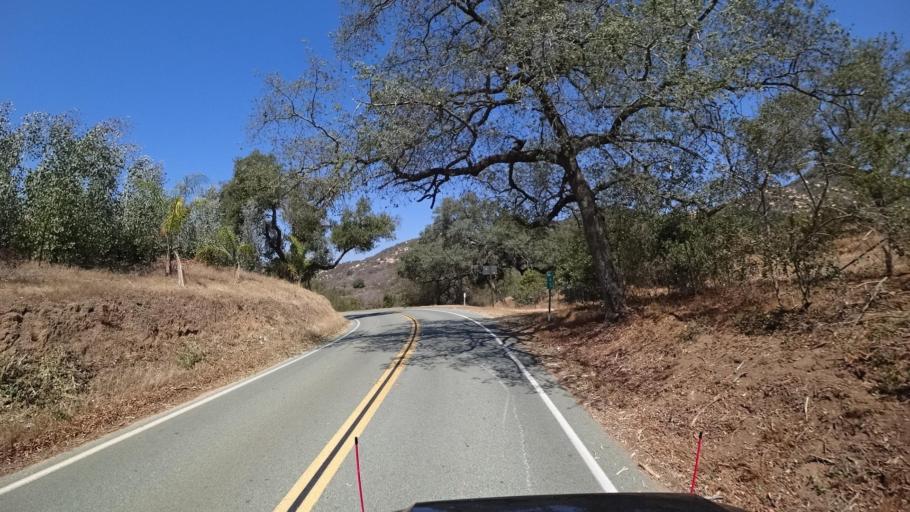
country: US
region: California
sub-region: San Diego County
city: Fallbrook
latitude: 33.4127
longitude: -117.2820
